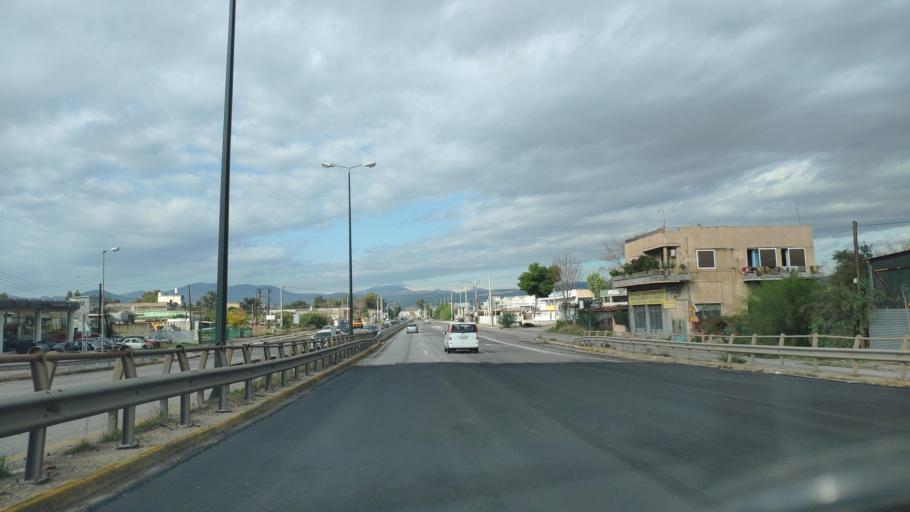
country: GR
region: Attica
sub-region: Nomarchia Dytikis Attikis
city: Aspropyrgos
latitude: 38.0440
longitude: 23.5827
